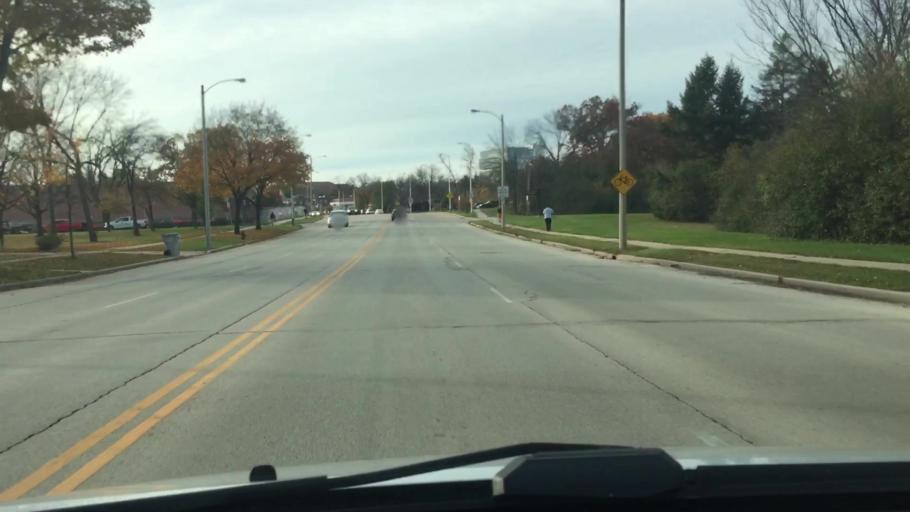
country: US
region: Wisconsin
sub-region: Milwaukee County
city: Wauwatosa
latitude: 43.0353
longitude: -88.0117
